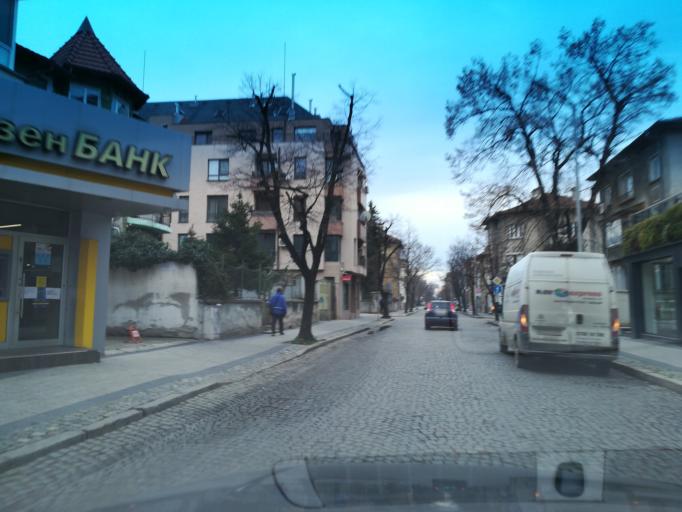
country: BG
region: Plovdiv
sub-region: Obshtina Plovdiv
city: Plovdiv
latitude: 42.1414
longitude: 24.7429
